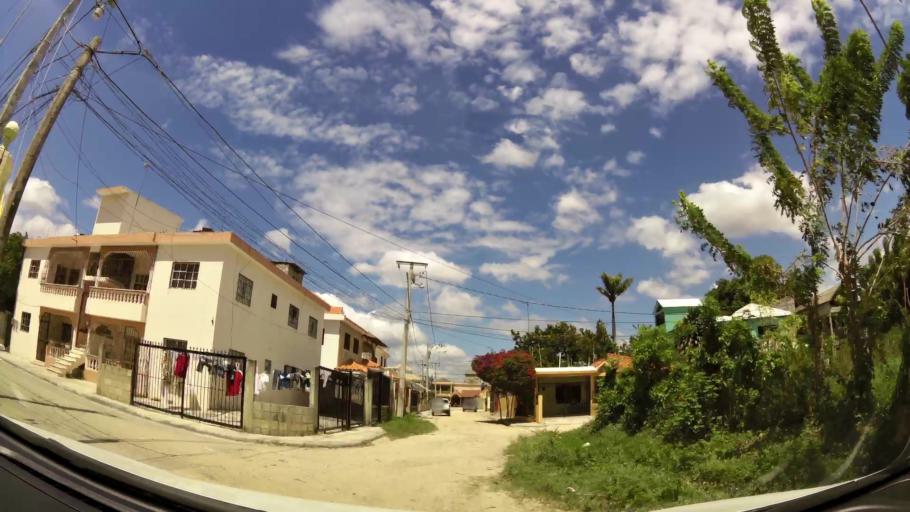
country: DO
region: San Cristobal
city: San Cristobal
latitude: 18.4089
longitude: -70.1008
